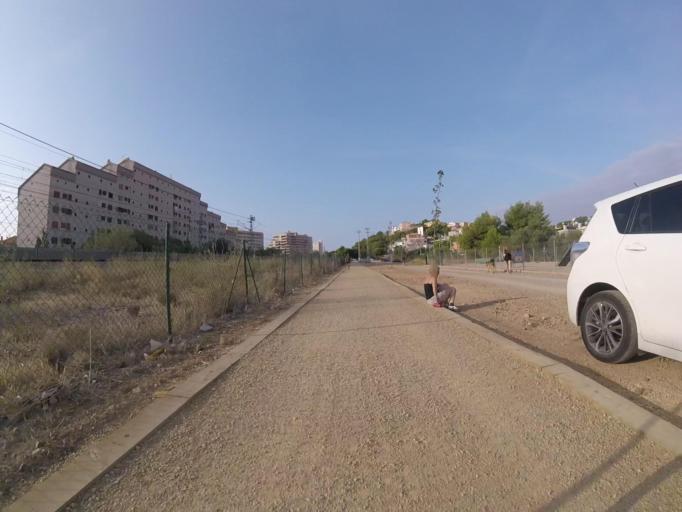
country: ES
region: Valencia
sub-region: Provincia de Castello
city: Orpesa/Oropesa del Mar
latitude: 40.0853
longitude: 0.1372
